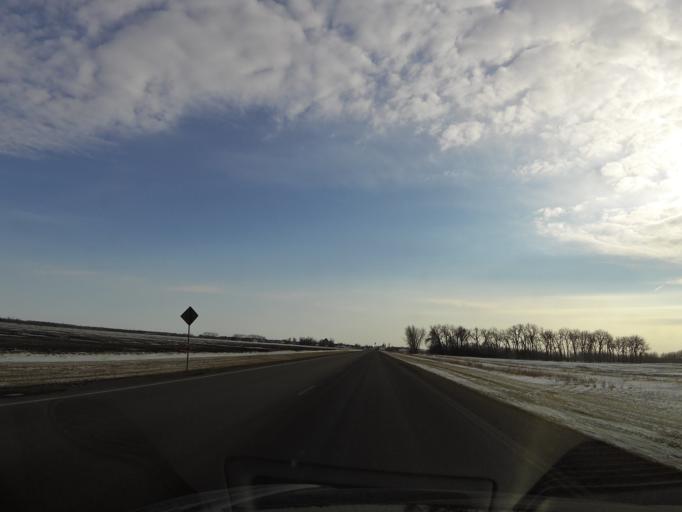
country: US
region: North Dakota
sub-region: Walsh County
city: Grafton
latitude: 48.5836
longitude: -97.1788
